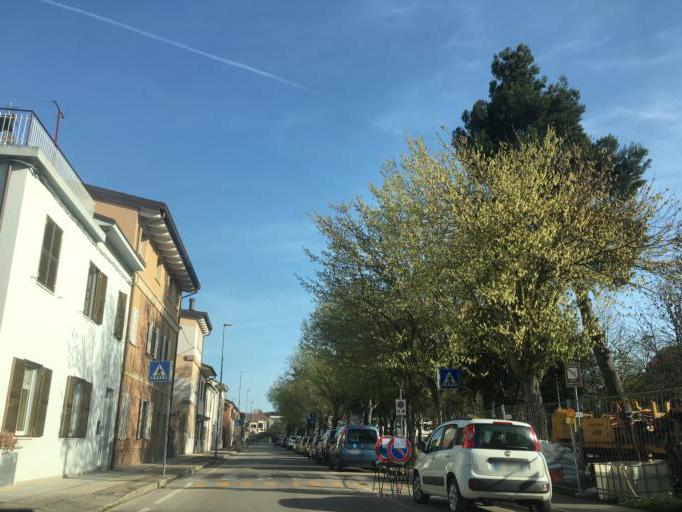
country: IT
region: The Marches
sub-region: Provincia di Pesaro e Urbino
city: Pesaro
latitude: 43.8964
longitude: 12.8882
